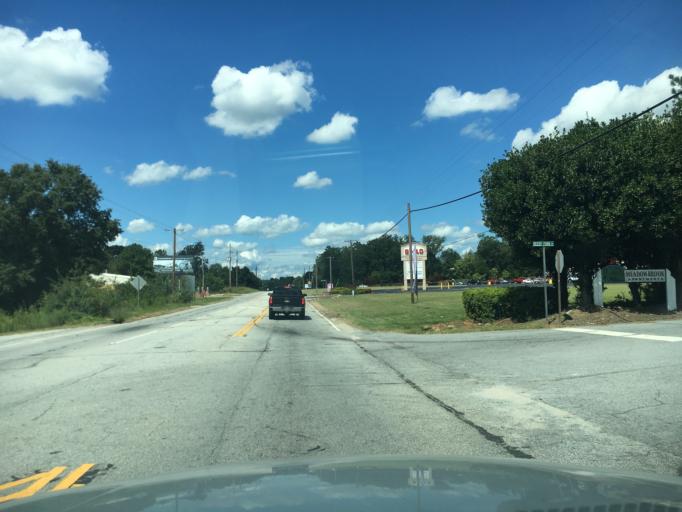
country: US
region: South Carolina
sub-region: Laurens County
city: Laurens
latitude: 34.4994
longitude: -82.0476
